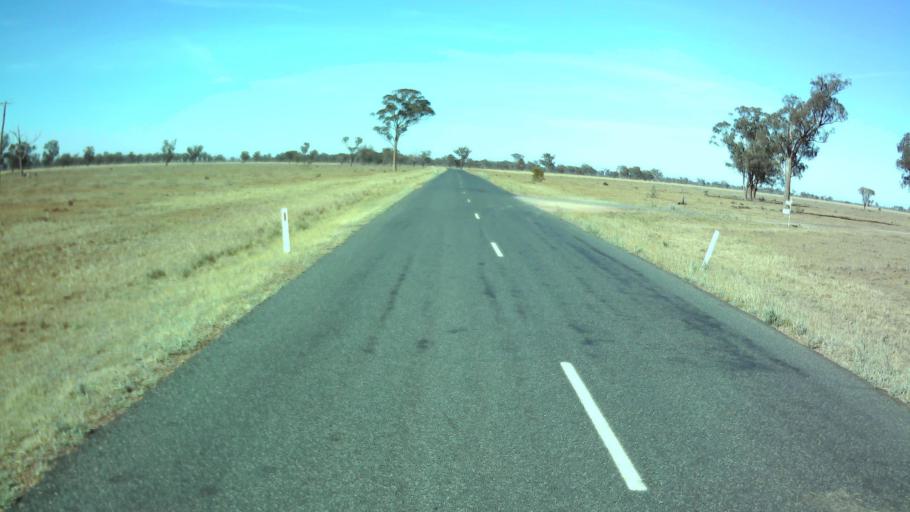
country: AU
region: New South Wales
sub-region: Weddin
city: Grenfell
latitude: -34.0481
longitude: 147.9217
